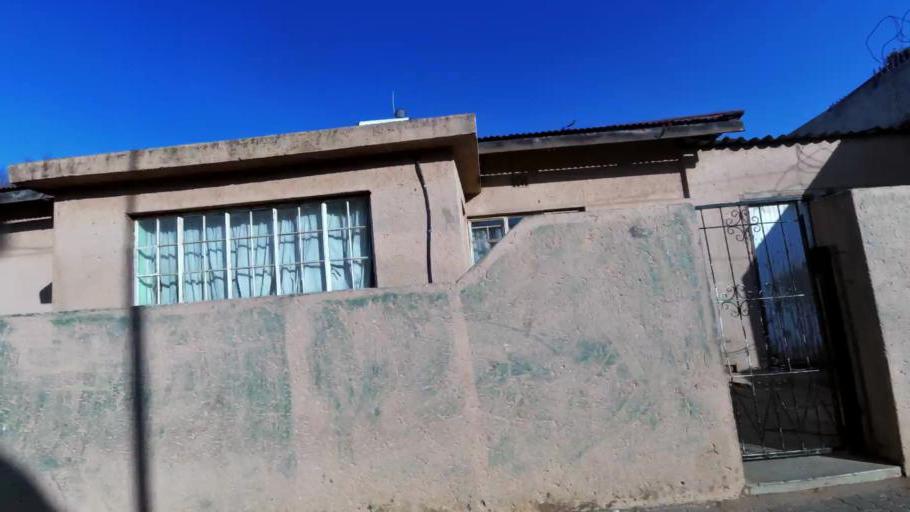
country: ZA
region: Gauteng
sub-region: City of Johannesburg Metropolitan Municipality
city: Johannesburg
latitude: -26.1929
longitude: 28.0179
